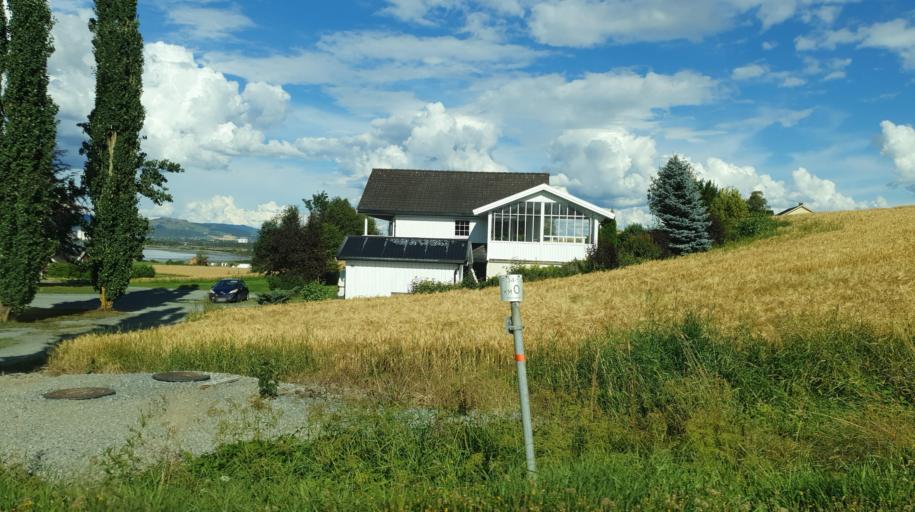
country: NO
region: Nord-Trondelag
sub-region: Verdal
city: Verdal
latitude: 63.7626
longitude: 11.4047
